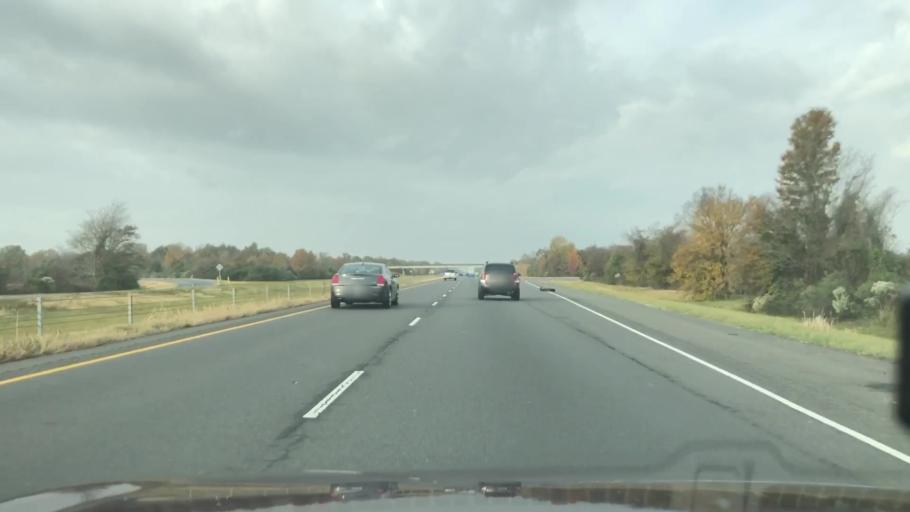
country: US
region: Louisiana
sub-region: Richland Parish
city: Delhi
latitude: 32.4561
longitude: -91.6220
